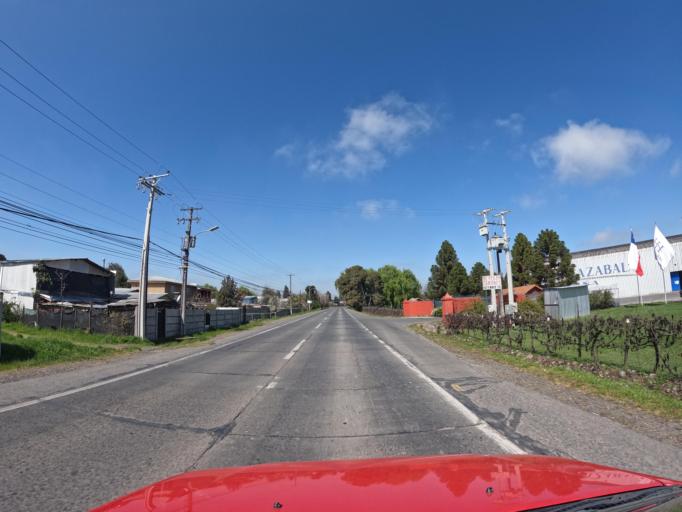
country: CL
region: Maule
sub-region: Provincia de Curico
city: Molina
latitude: -35.0663
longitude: -71.2560
